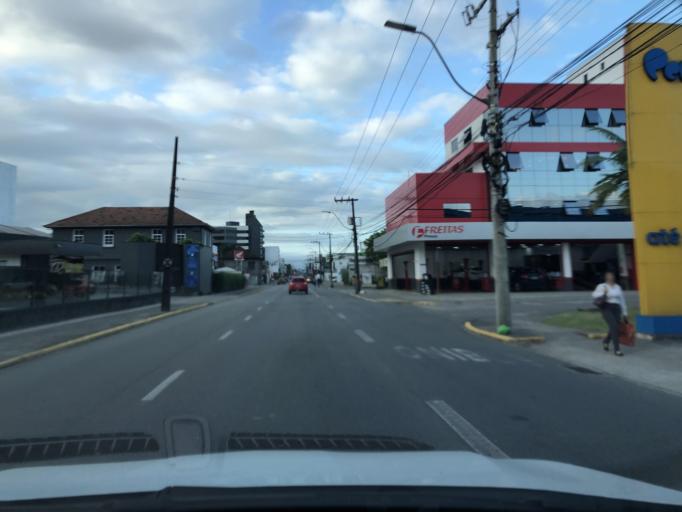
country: BR
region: Santa Catarina
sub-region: Joinville
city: Joinville
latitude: -26.2920
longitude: -48.8483
